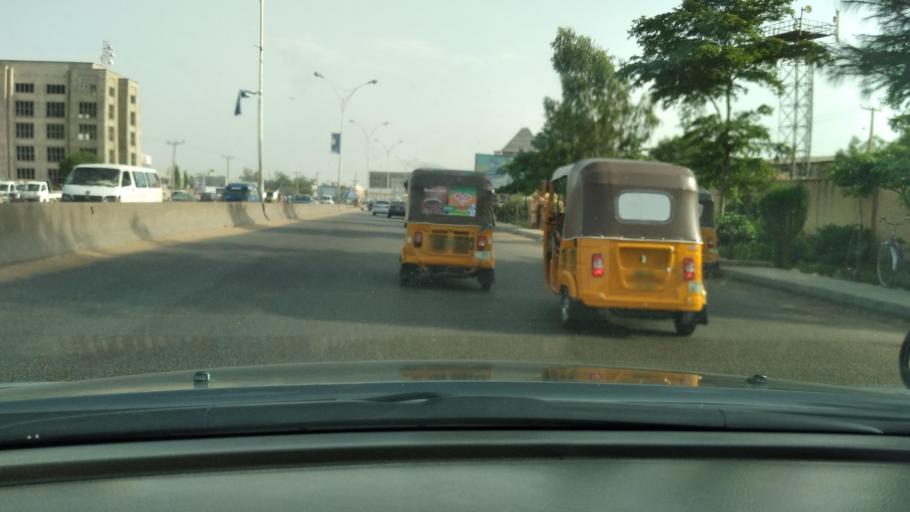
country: NG
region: Kano
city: Kano
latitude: 11.9466
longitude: 8.5657
